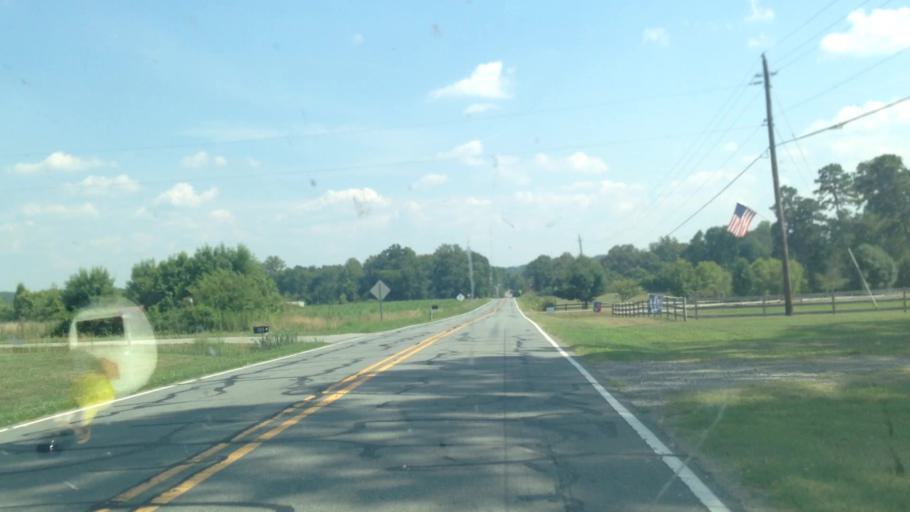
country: US
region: North Carolina
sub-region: Stokes County
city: Walnut Cove
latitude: 36.3396
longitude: -80.0513
